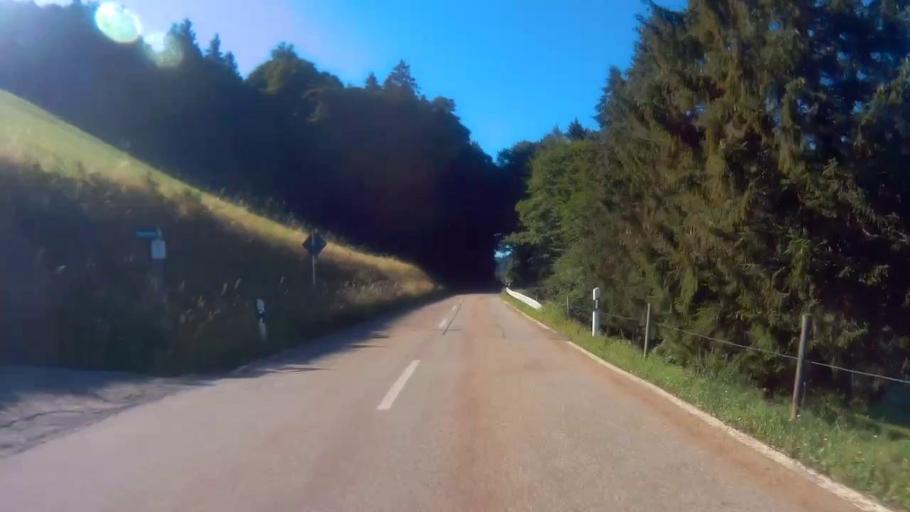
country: DE
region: Baden-Wuerttemberg
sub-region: Freiburg Region
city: Wieden
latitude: 47.8476
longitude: 7.8663
